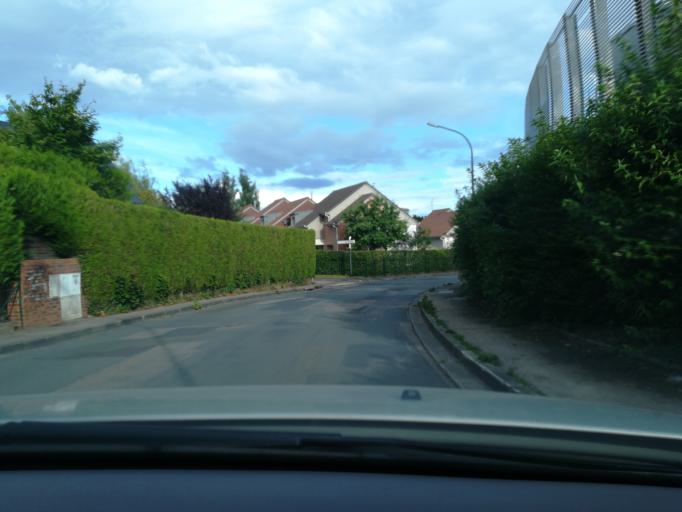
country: FR
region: Haute-Normandie
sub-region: Departement de la Seine-Maritime
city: Mont-Saint-Aignan
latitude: 49.4762
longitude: 1.1085
